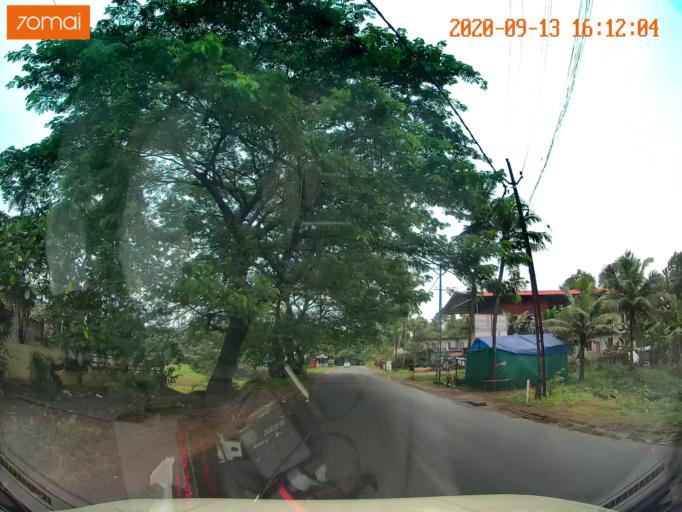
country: IN
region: Kerala
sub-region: Kottayam
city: Palackattumala
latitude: 9.6868
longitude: 76.6158
